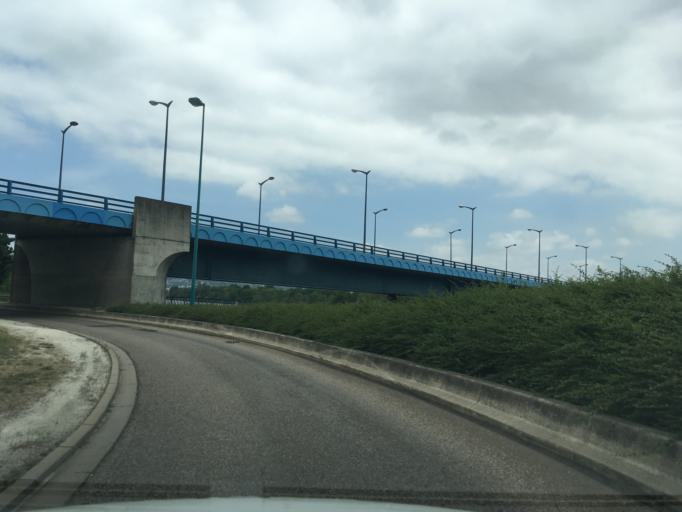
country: FR
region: Lorraine
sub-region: Departement de Meurthe-et-Moselle
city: Tomblaine
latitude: 48.6776
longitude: 6.2088
